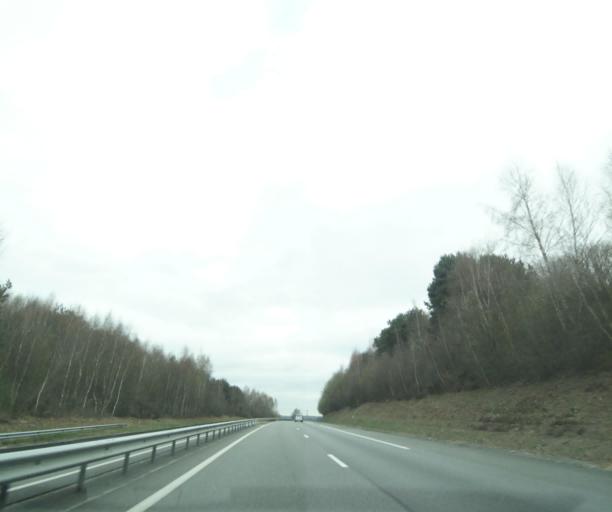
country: FR
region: Limousin
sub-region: Departement de la Haute-Vienne
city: Saint-Germain-les-Belles
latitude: 45.5153
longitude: 1.5165
